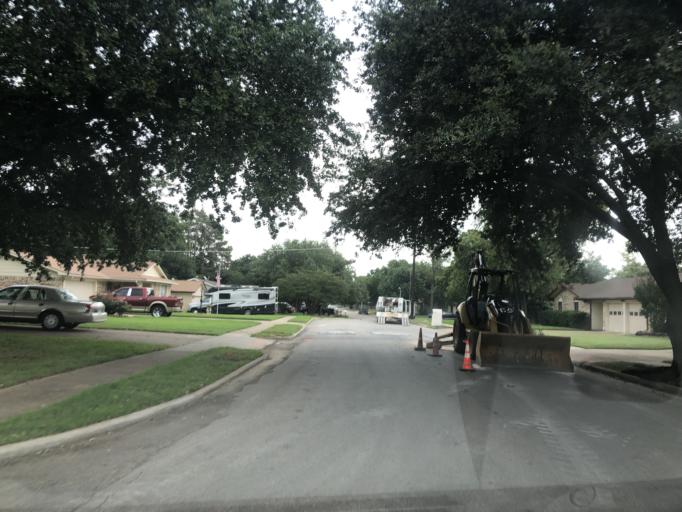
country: US
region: Texas
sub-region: Dallas County
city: Irving
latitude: 32.7854
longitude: -96.9692
